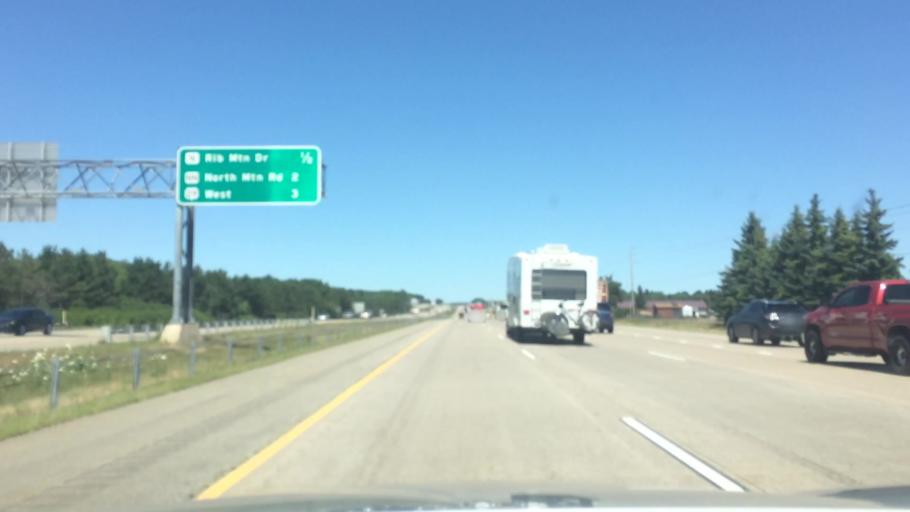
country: US
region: Wisconsin
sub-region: Marathon County
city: Rothschild
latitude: 44.9028
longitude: -89.6443
